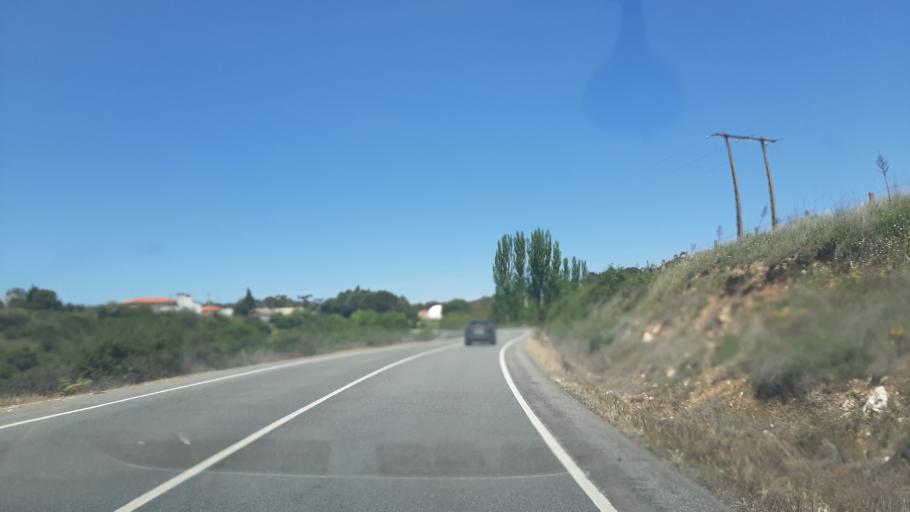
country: ES
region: Castille and Leon
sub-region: Provincia de Salamanca
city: Guijo de Avila
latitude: 40.5528
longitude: -5.6386
